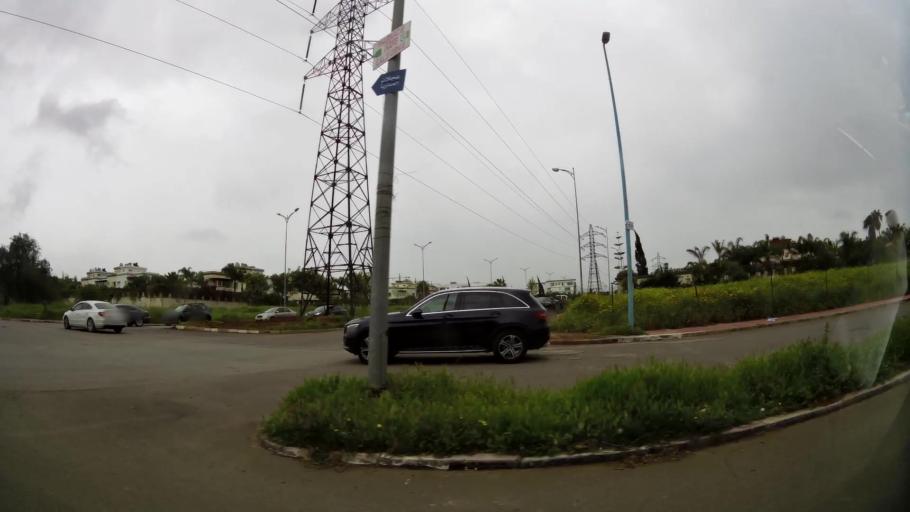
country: MA
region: Grand Casablanca
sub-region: Casablanca
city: Casablanca
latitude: 33.5258
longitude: -7.6171
